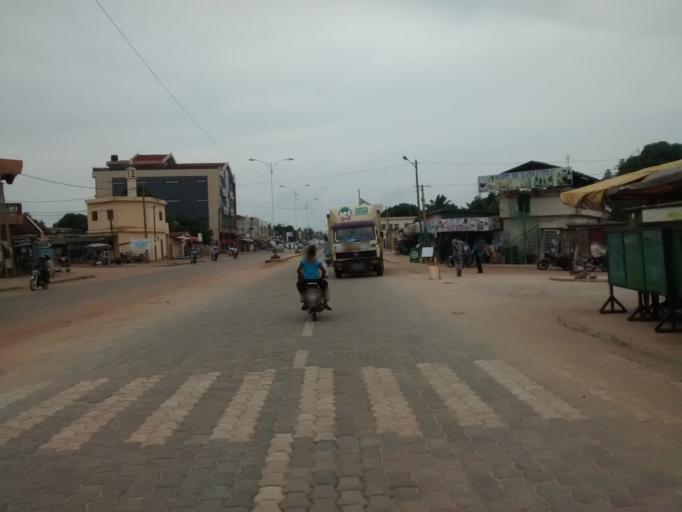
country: TG
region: Maritime
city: Lome
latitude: 6.1778
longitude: 1.1967
